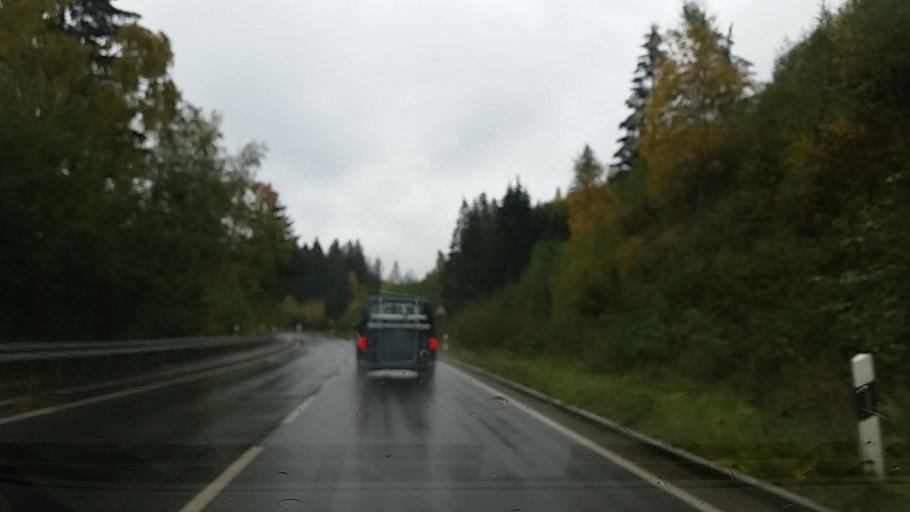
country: DE
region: Lower Saxony
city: Schulenberg im Oberharz
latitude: 51.8376
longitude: 10.4550
